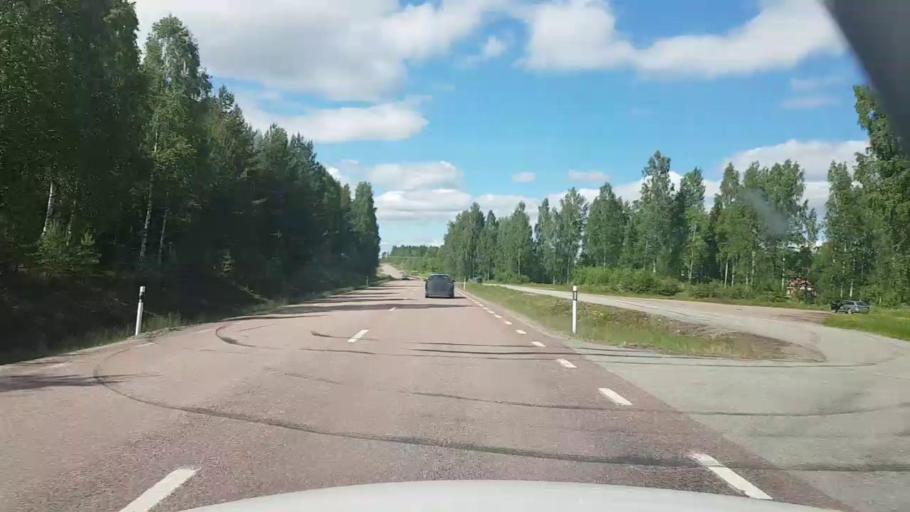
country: SE
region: Gaevleborg
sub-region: Ljusdals Kommun
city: Jaervsoe
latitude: 61.7615
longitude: 16.1596
